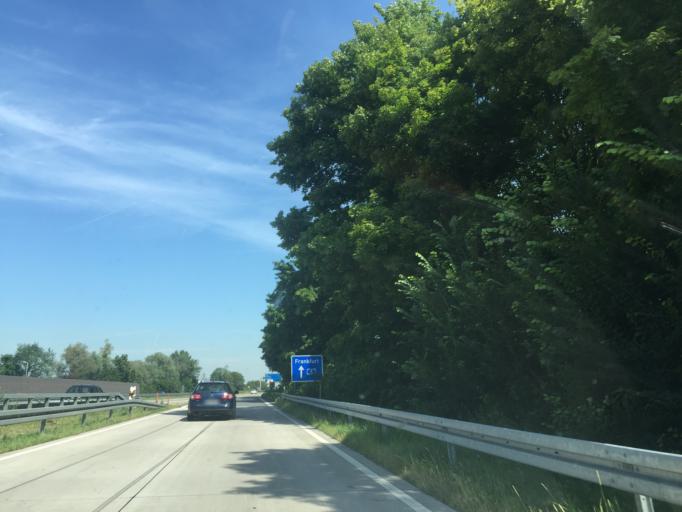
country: DE
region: Baden-Wuerttemberg
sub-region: Karlsruhe Region
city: Weinheim
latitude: 49.5329
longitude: 8.6331
